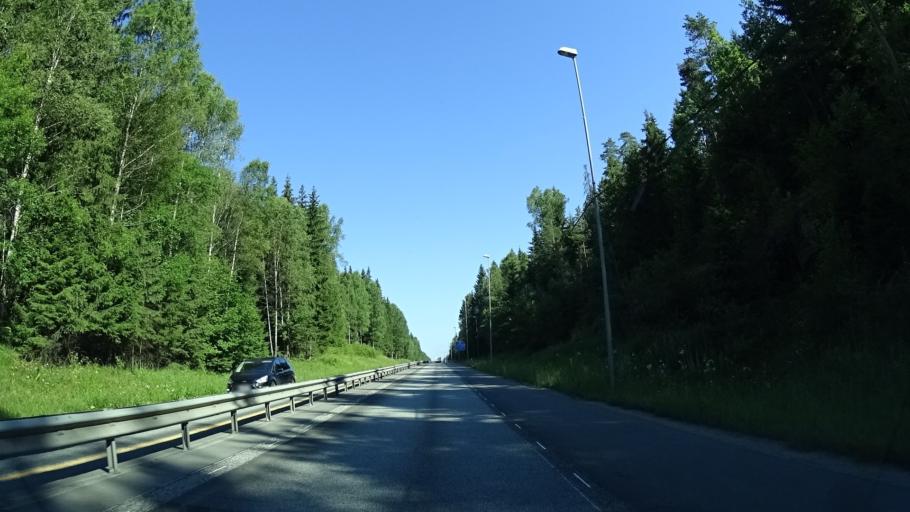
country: NO
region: Akershus
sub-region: Oppegard
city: Kolbotn
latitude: 59.7664
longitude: 10.7750
